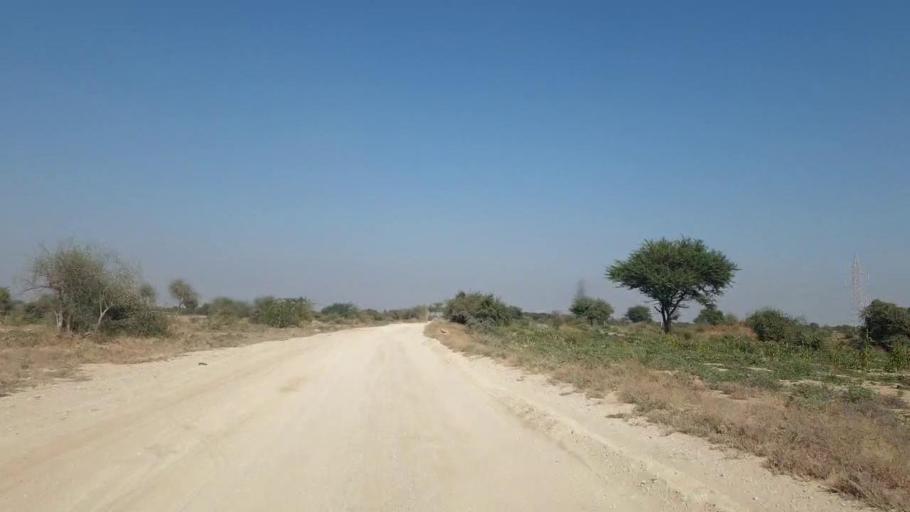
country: PK
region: Sindh
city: Jamshoro
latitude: 25.2953
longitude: 67.8142
